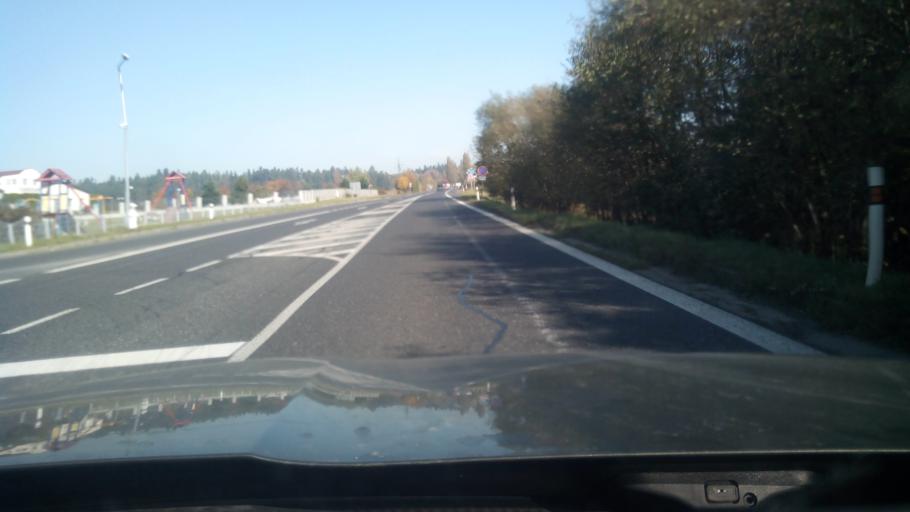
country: CZ
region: Central Bohemia
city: Milin
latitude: 49.6509
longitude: 14.0542
